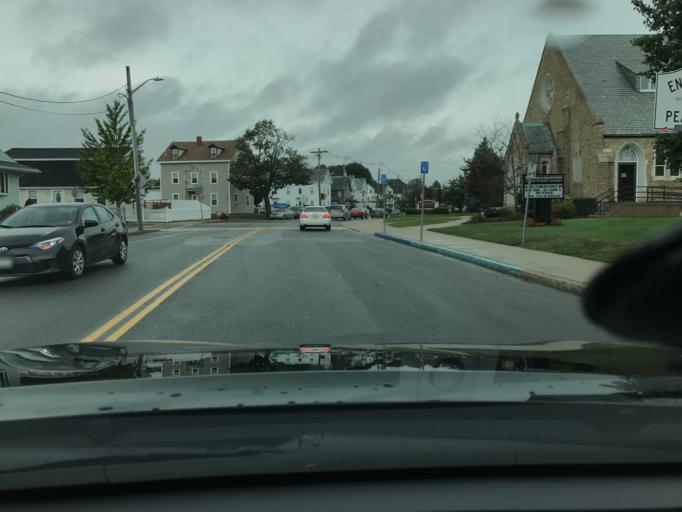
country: US
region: Massachusetts
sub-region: Essex County
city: Peabody
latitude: 42.5323
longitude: -70.9127
